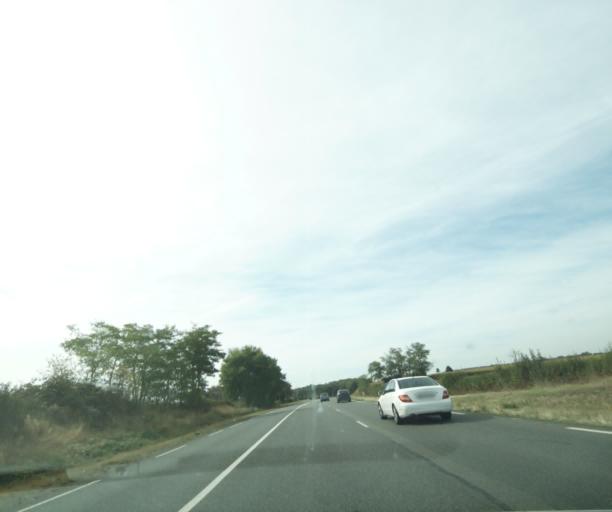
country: FR
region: Auvergne
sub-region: Departement de l'Allier
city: Lapalisse
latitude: 46.2412
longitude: 3.6102
